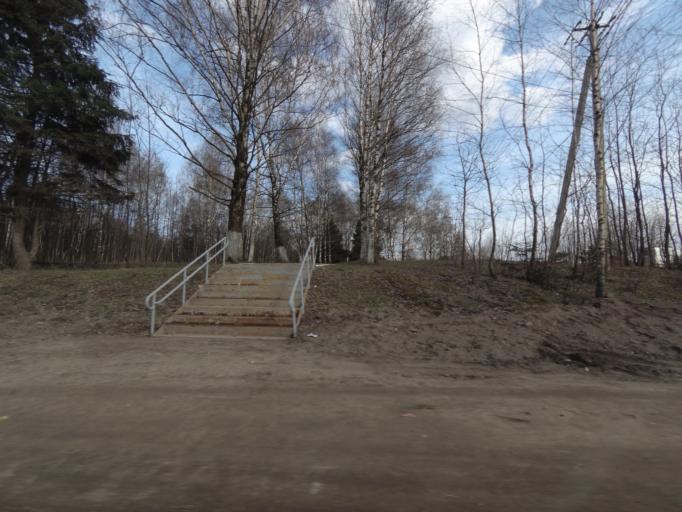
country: RU
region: Moskovskaya
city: Lobnya
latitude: 55.9977
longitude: 37.4223
